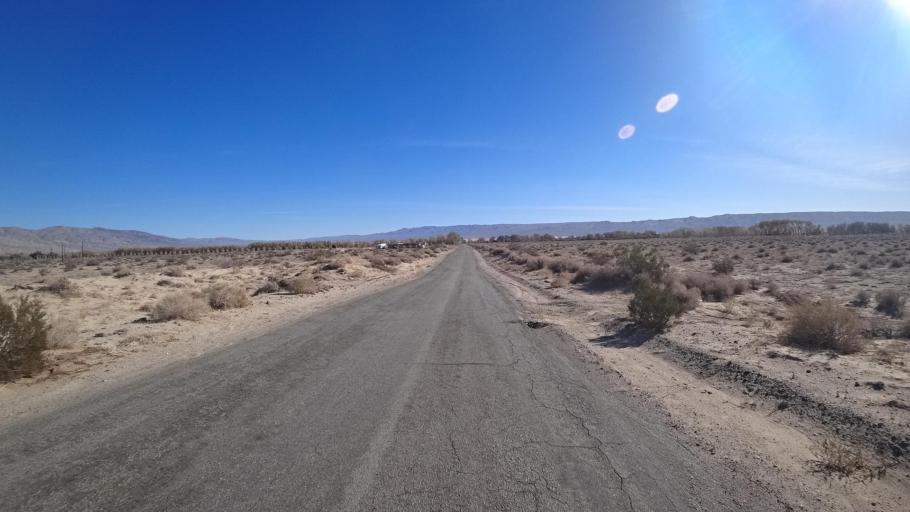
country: US
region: California
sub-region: Kern County
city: California City
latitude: 35.3154
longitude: -117.9362
